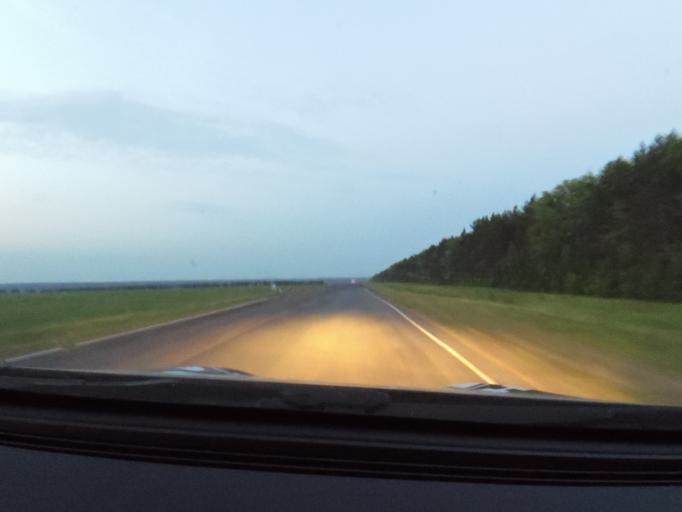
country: RU
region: Bashkortostan
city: Duvan
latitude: 56.0764
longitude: 58.1277
